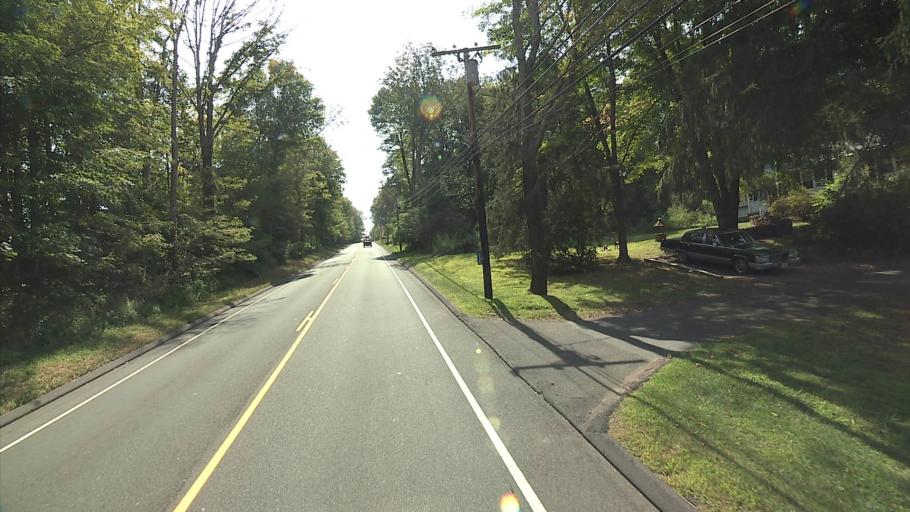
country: US
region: Connecticut
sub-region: Middlesex County
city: Durham
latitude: 41.4593
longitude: -72.6755
